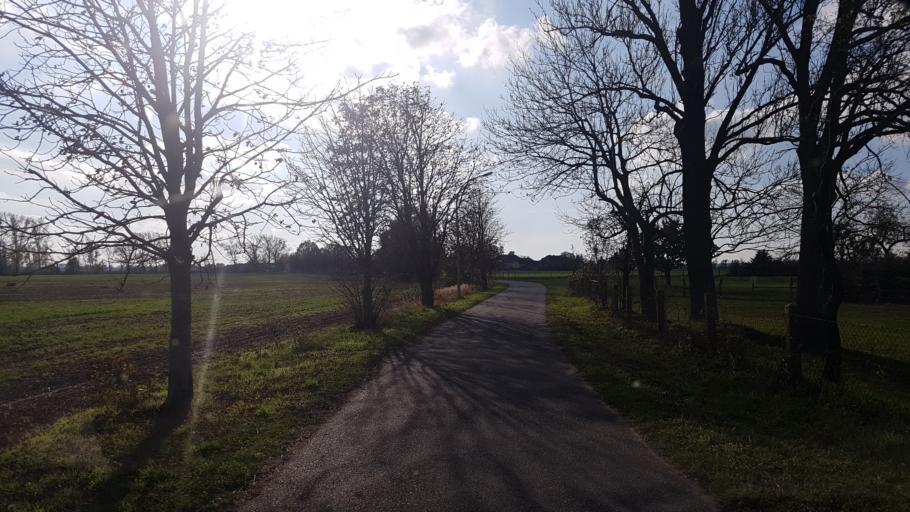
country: DE
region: Brandenburg
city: Schonewalde
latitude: 51.6974
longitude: 13.5735
